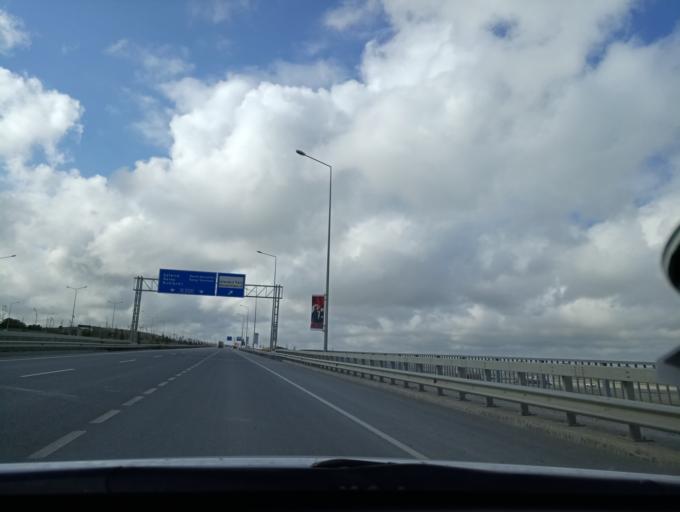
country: TR
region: Istanbul
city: Durusu
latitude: 41.2454
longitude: 28.7611
